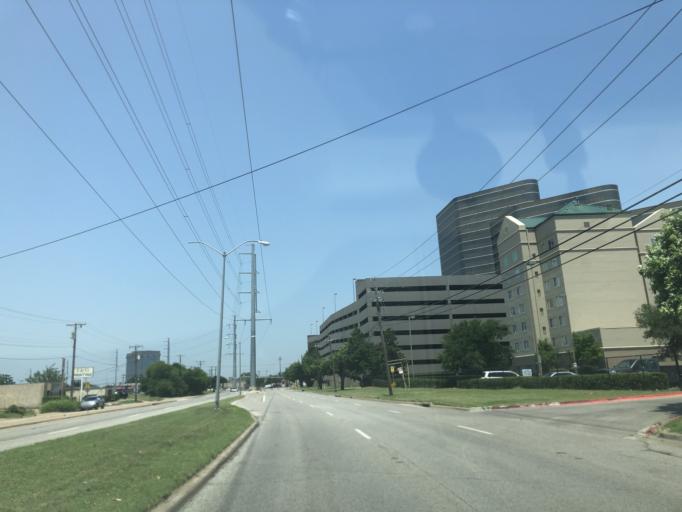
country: US
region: Texas
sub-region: Dallas County
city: Dallas
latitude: 32.8080
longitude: -96.8474
